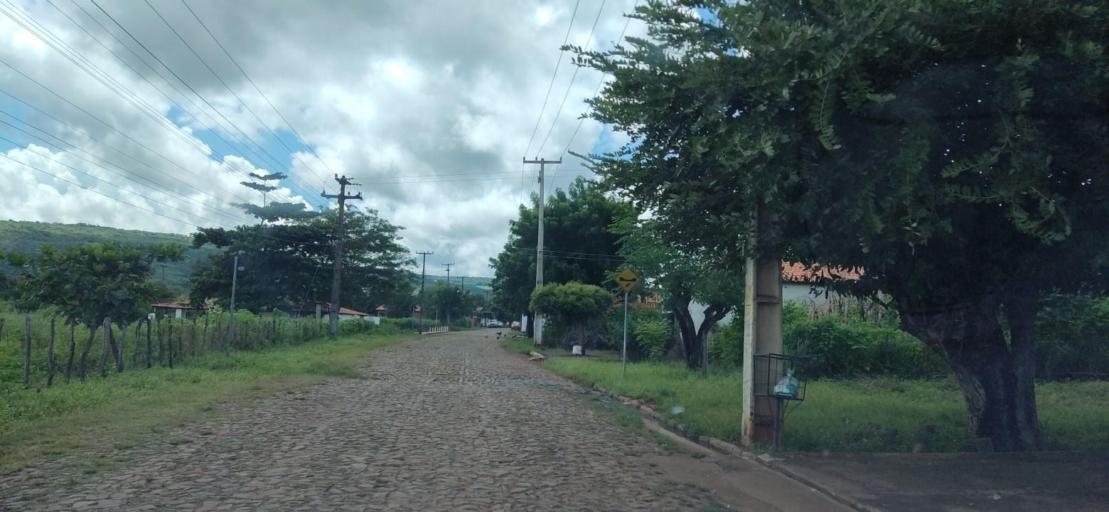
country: BR
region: Piaui
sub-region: Valenca Do Piaui
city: Valenca do Piaui
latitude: -6.1116
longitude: -41.8006
